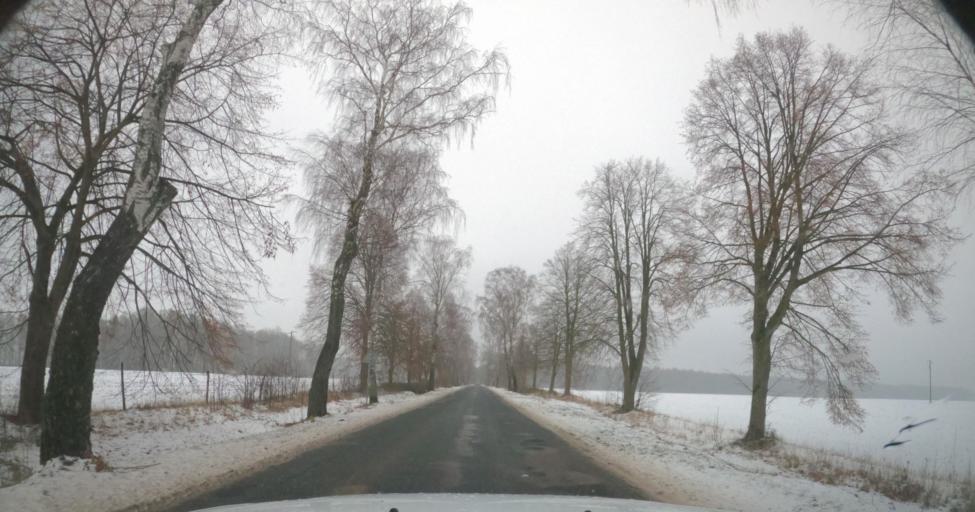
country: PL
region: West Pomeranian Voivodeship
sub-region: Powiat gryficki
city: Gryfice
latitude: 53.9084
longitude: 15.2511
